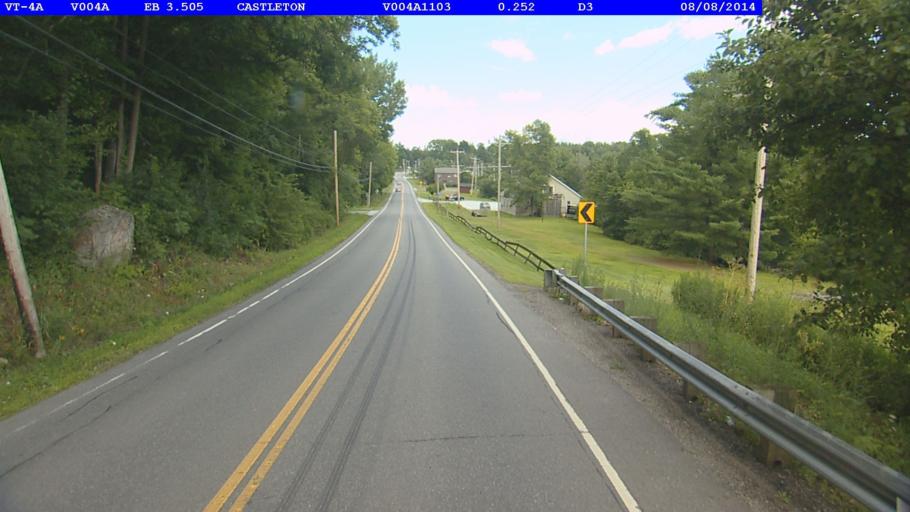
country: US
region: Vermont
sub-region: Rutland County
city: Fair Haven
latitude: 43.6028
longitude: -73.2375
